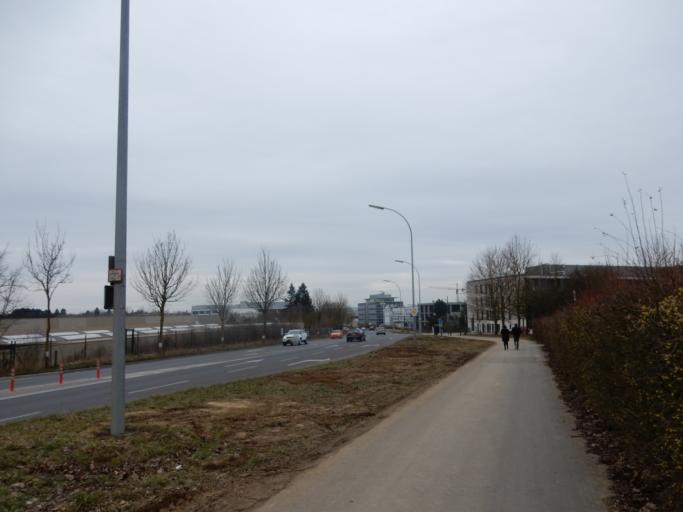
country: LU
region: Luxembourg
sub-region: Canton de Luxembourg
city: Luxembourg
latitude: 49.5798
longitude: 6.1139
